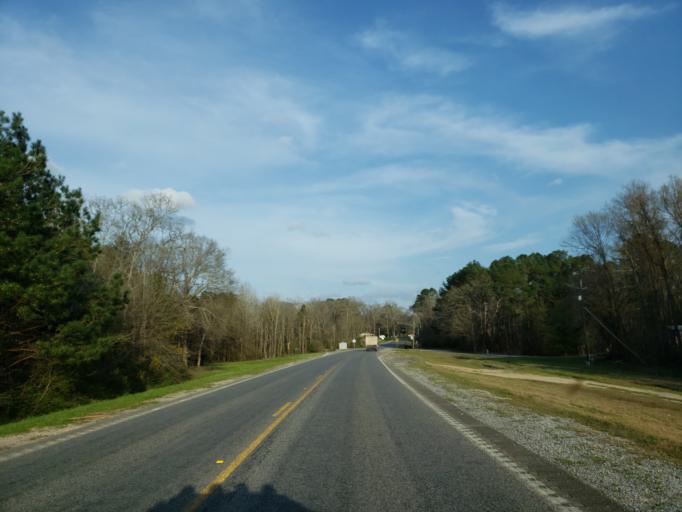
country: US
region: Mississippi
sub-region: Clarke County
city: Stonewall
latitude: 32.1762
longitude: -88.8162
